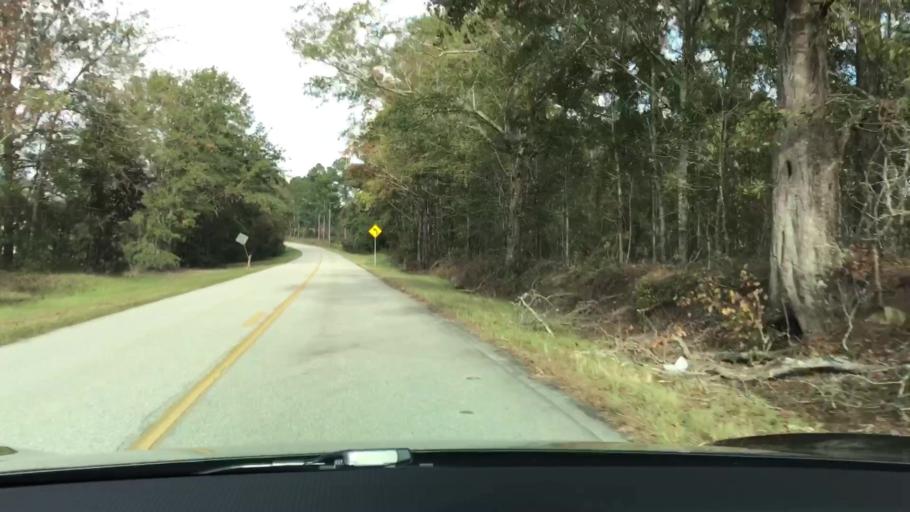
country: US
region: Georgia
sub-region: Jefferson County
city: Wadley
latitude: 32.8044
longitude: -82.3884
